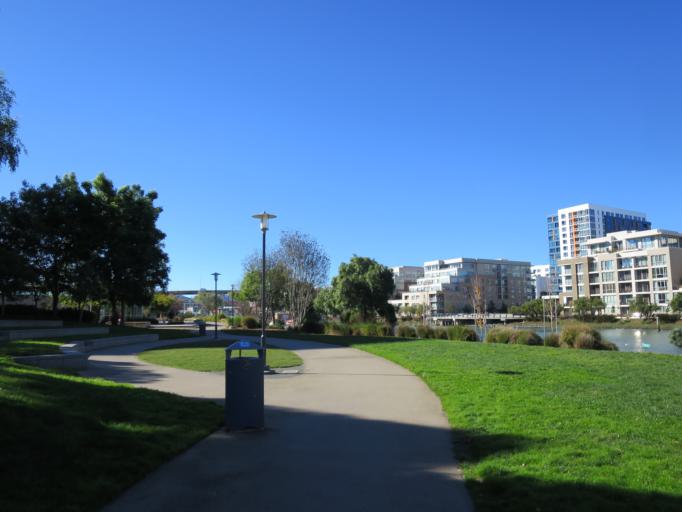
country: US
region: California
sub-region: San Francisco County
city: San Francisco
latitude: 37.7736
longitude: -122.3931
